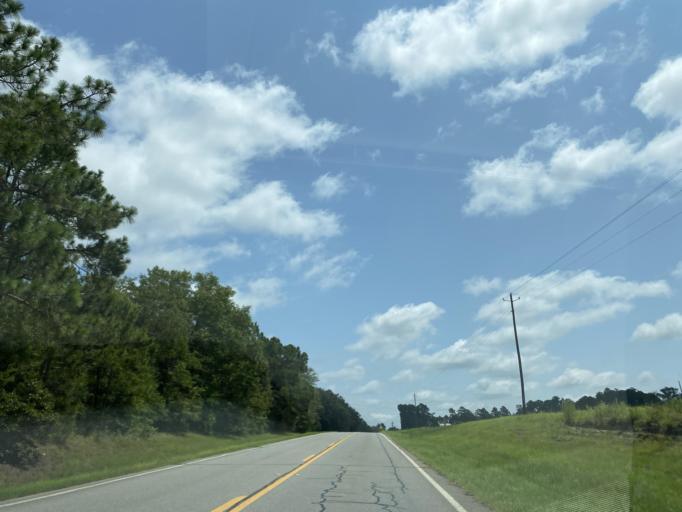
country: US
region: Georgia
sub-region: Wilcox County
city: Abbeville
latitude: 32.0072
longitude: -83.1249
